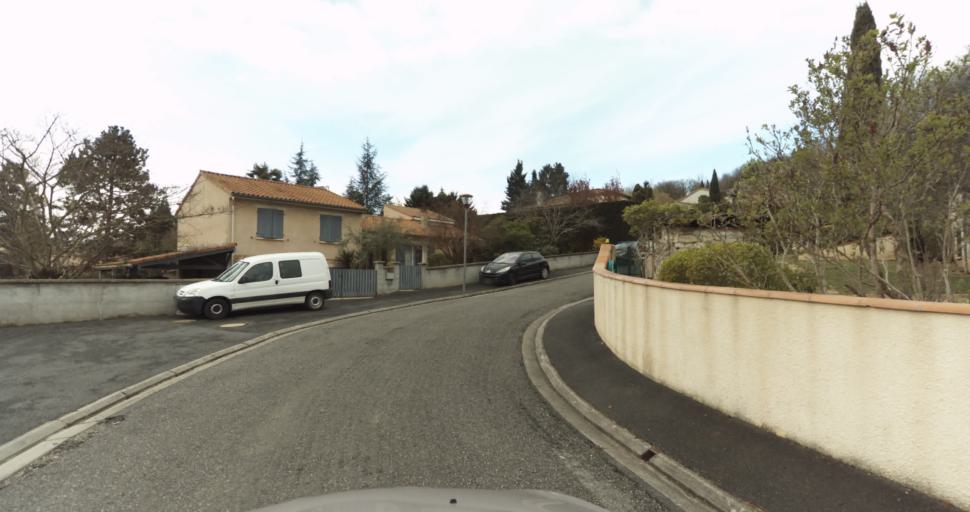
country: FR
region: Midi-Pyrenees
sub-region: Departement du Tarn
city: Puygouzon
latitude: 43.9005
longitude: 2.1820
